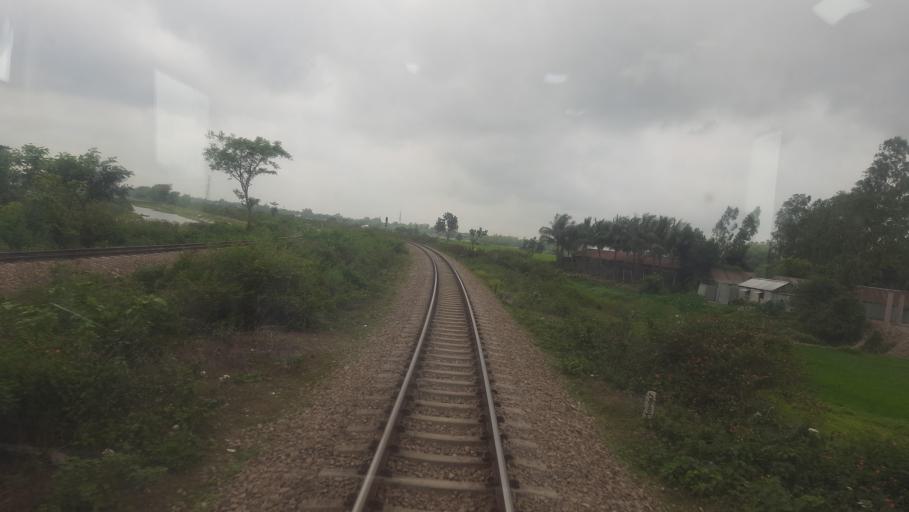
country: BD
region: Dhaka
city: Bhairab Bazar
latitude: 24.0492
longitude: 90.9691
